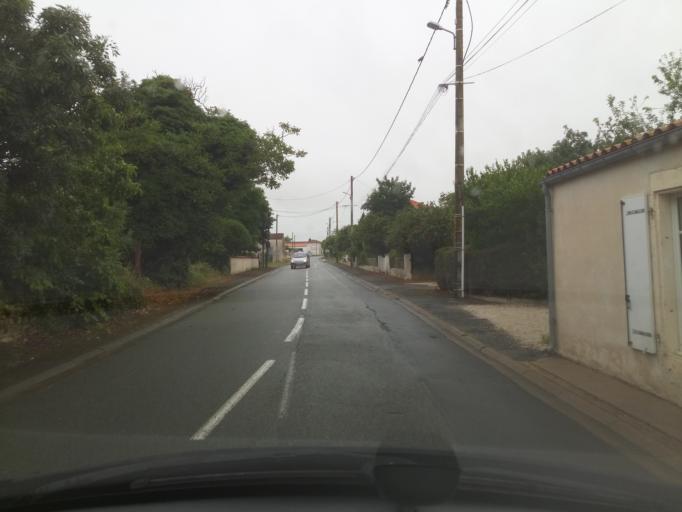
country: FR
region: Poitou-Charentes
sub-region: Departement de la Charente-Maritime
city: Andilly
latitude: 46.2325
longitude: -0.9983
